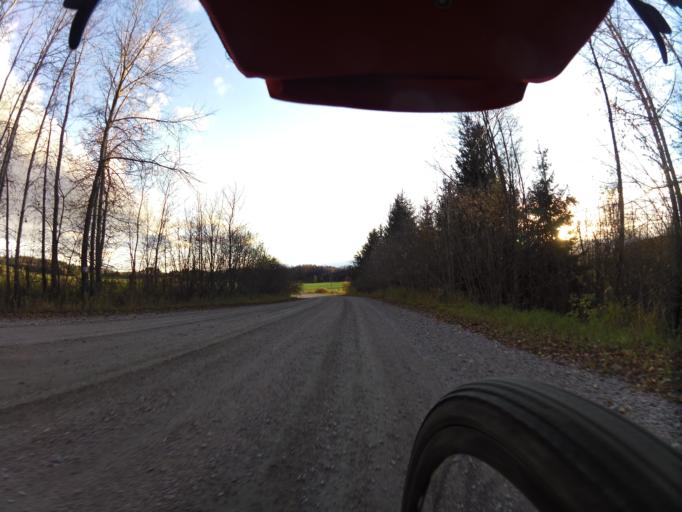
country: CA
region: Quebec
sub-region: Outaouais
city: Shawville
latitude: 45.6512
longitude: -76.3190
